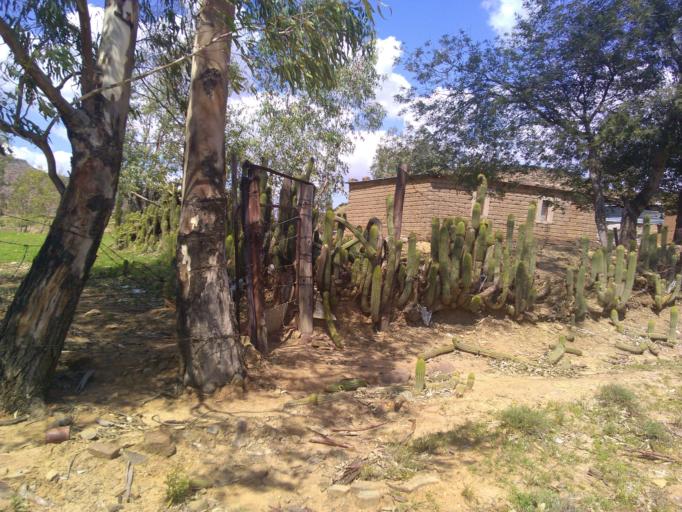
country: LS
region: Quthing
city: Quthing
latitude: -30.3389
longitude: 27.5302
